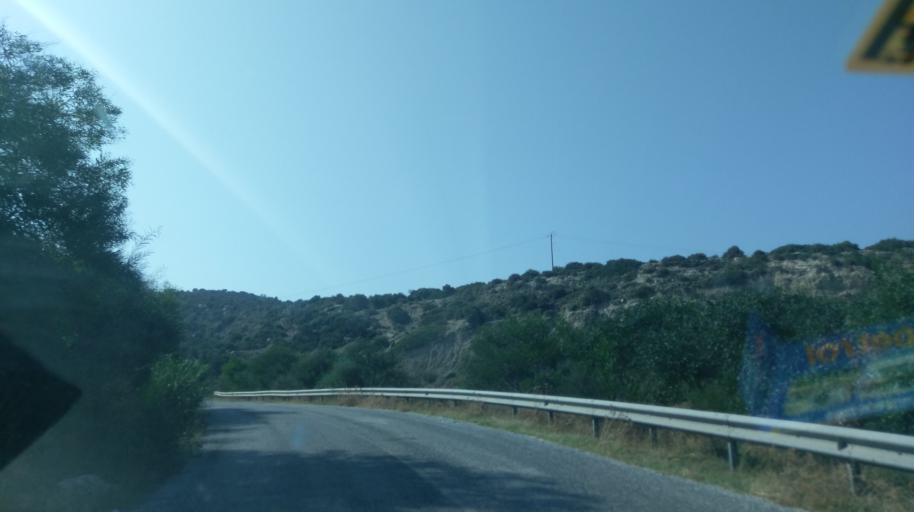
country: CY
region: Keryneia
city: Lapithos
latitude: 35.3575
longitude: 33.0480
